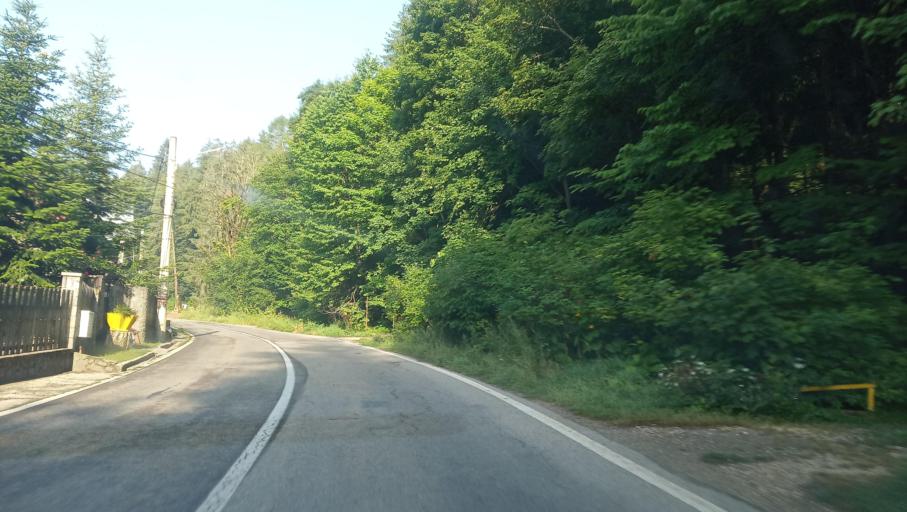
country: RO
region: Prahova
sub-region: Oras Sinaia
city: Sinaia
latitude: 45.3272
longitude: 25.5381
